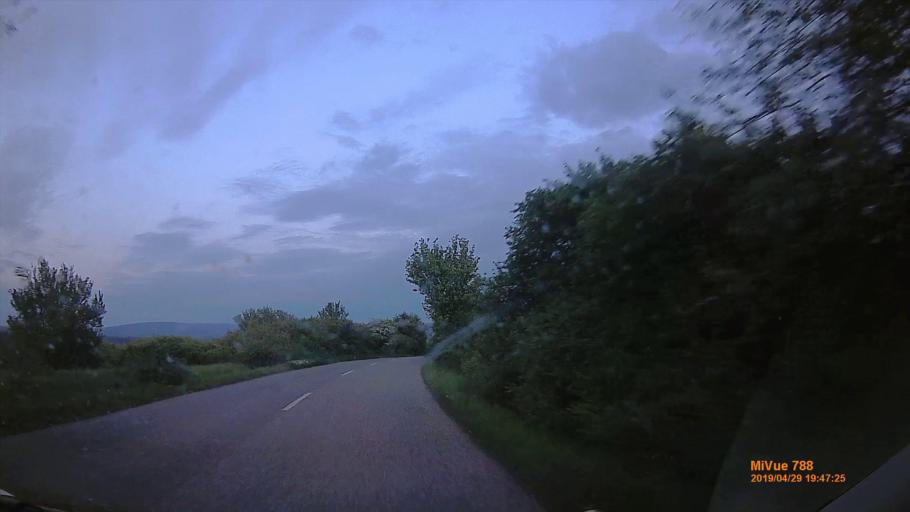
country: HU
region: Nograd
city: Retsag
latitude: 47.8847
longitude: 19.1197
